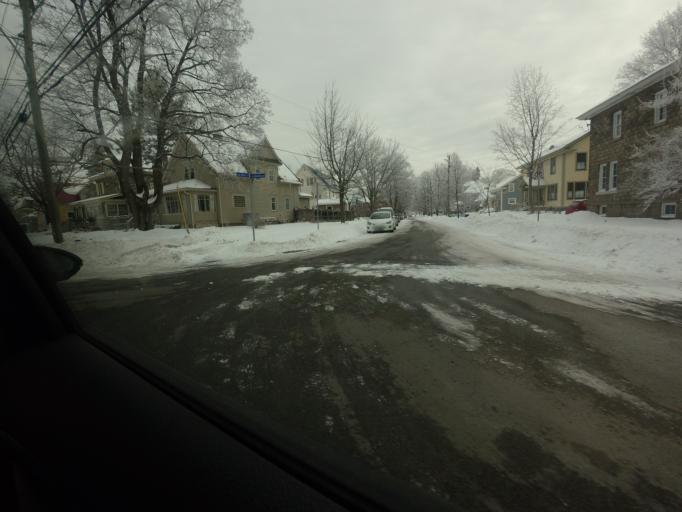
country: CA
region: New Brunswick
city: Fredericton
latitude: 45.9512
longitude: -66.6377
